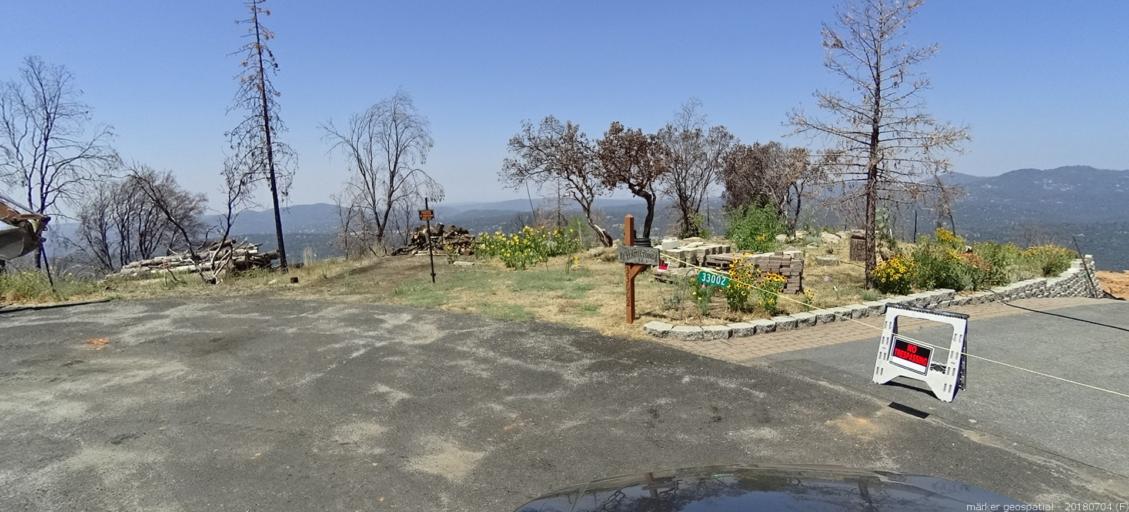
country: US
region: California
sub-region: Fresno County
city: Auberry
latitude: 37.2303
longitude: -119.4711
